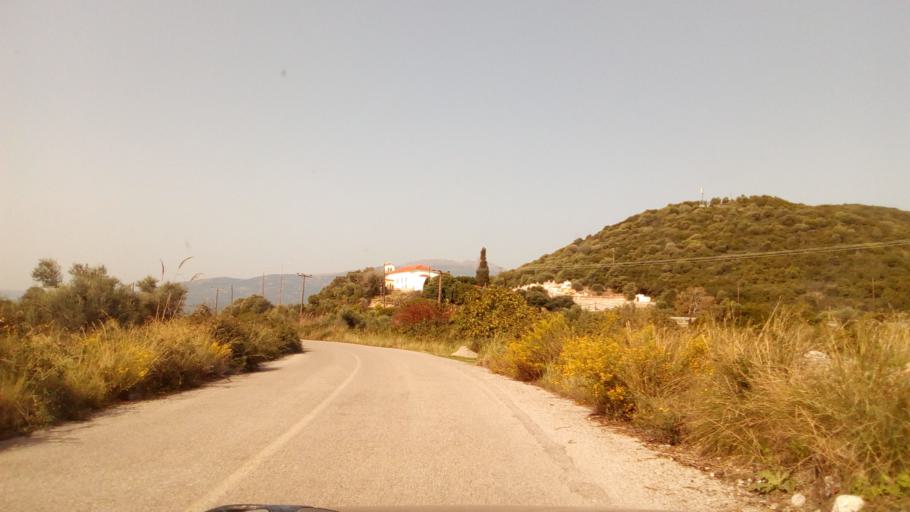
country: GR
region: West Greece
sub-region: Nomos Aitolias kai Akarnanias
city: Nafpaktos
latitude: 38.4032
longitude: 21.9188
